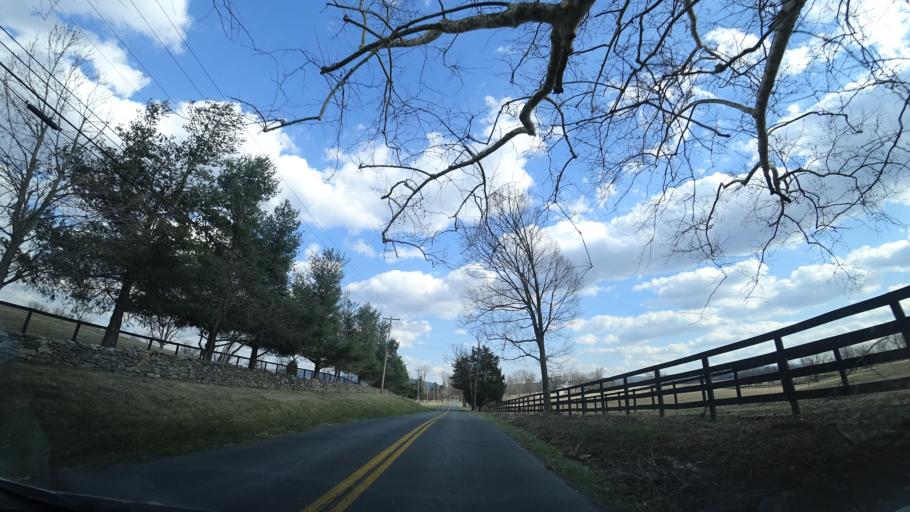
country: US
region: Virginia
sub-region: Warren County
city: Shenandoah Farms
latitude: 39.0610
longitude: -78.0261
